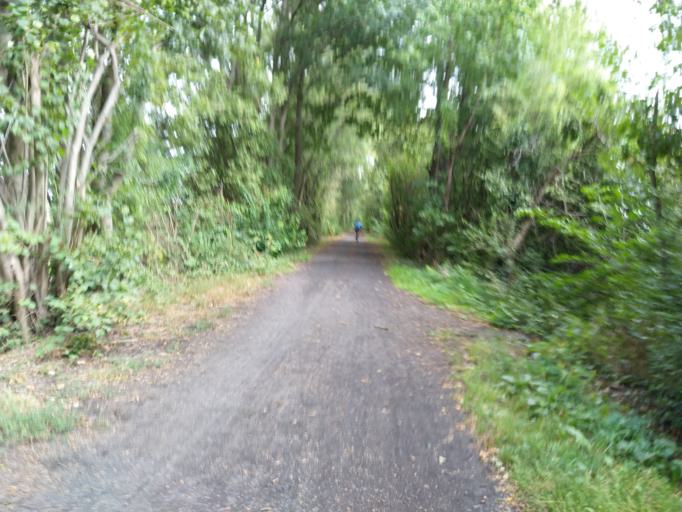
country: BE
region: Wallonia
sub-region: Province de Liege
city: Aubel
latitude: 50.7085
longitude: 5.8691
